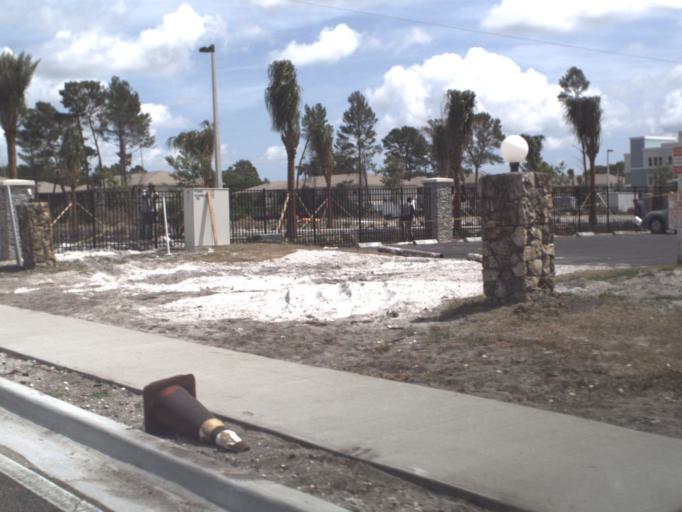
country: US
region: Florida
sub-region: Brevard County
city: Cocoa
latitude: 28.3842
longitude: -80.7550
